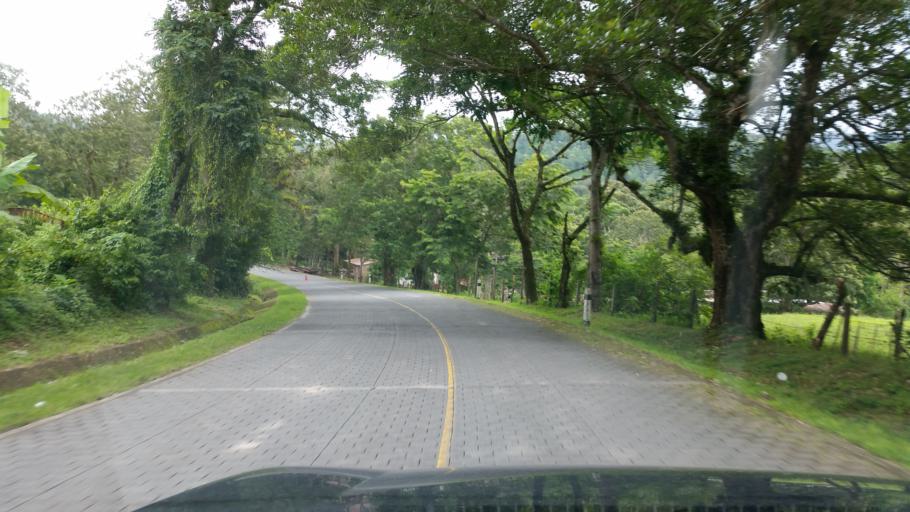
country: NI
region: Jinotega
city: Jinotega
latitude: 13.1926
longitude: -85.7326
